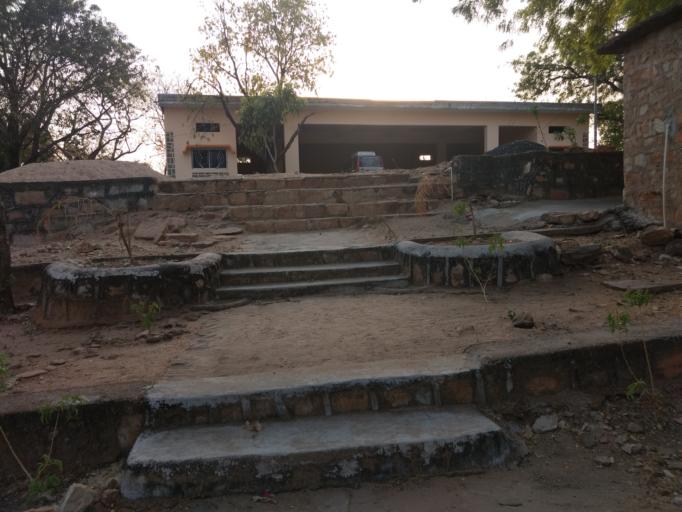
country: IN
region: Maharashtra
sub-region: Bhandara
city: Pauni
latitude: 20.5867
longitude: 79.7848
